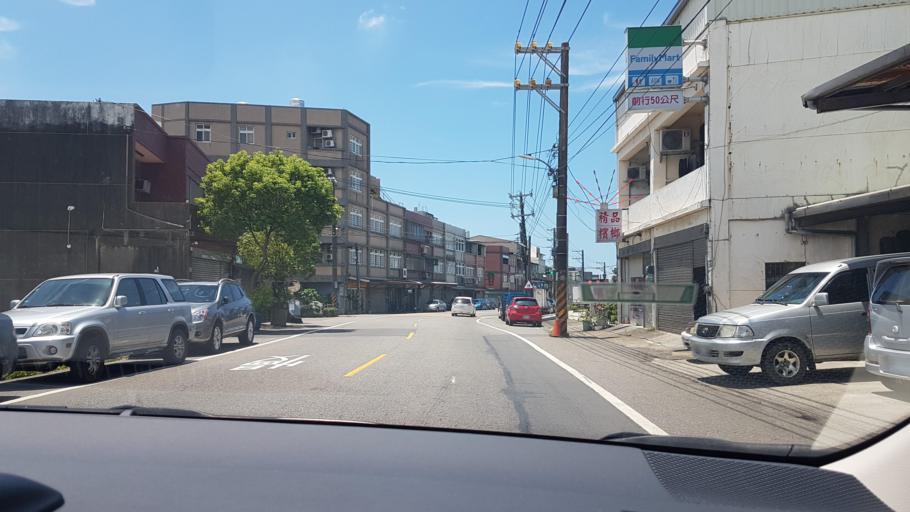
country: TW
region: Taiwan
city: Taoyuan City
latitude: 25.0867
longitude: 121.2829
